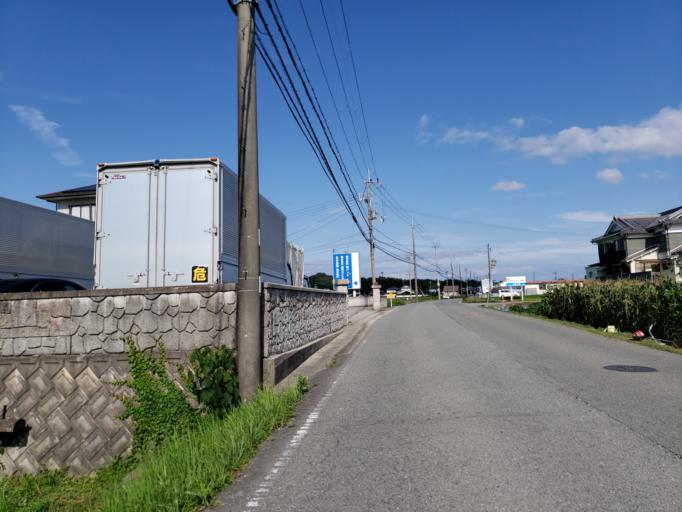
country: JP
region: Hyogo
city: Himeji
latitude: 34.9093
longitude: 134.7777
